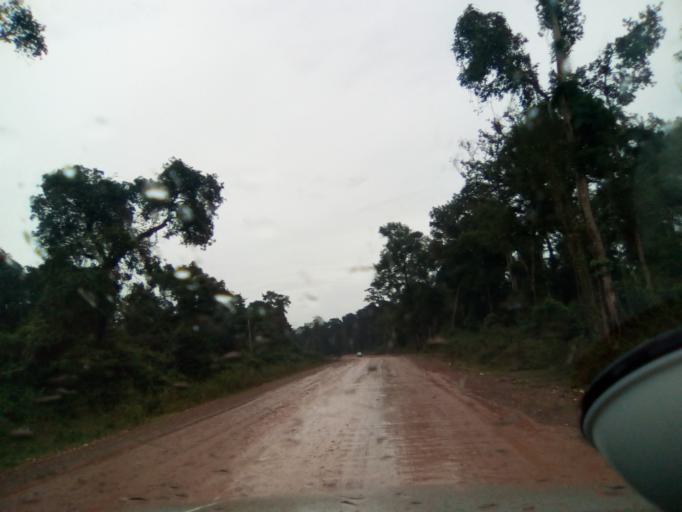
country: LA
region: Attapu
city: Attapu
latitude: 14.6856
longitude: 106.5489
